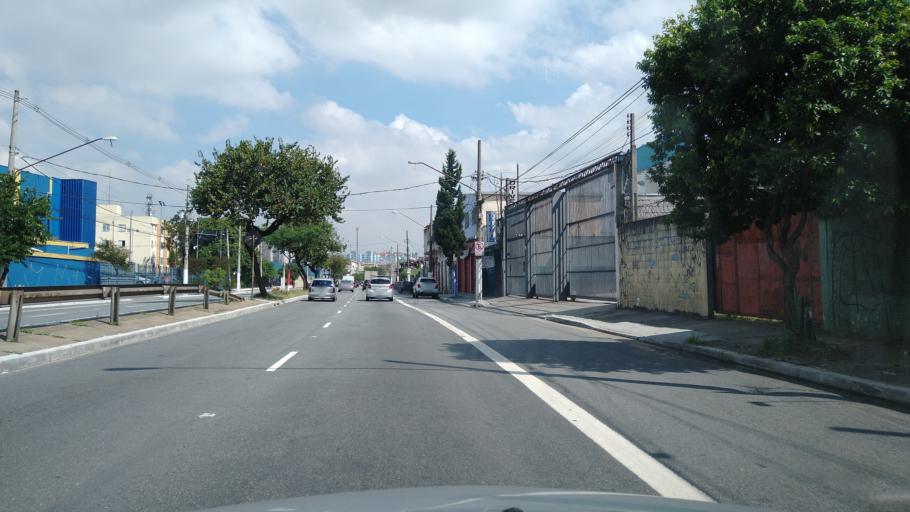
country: BR
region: Sao Paulo
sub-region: Guarulhos
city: Guarulhos
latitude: -23.4877
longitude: -46.5044
